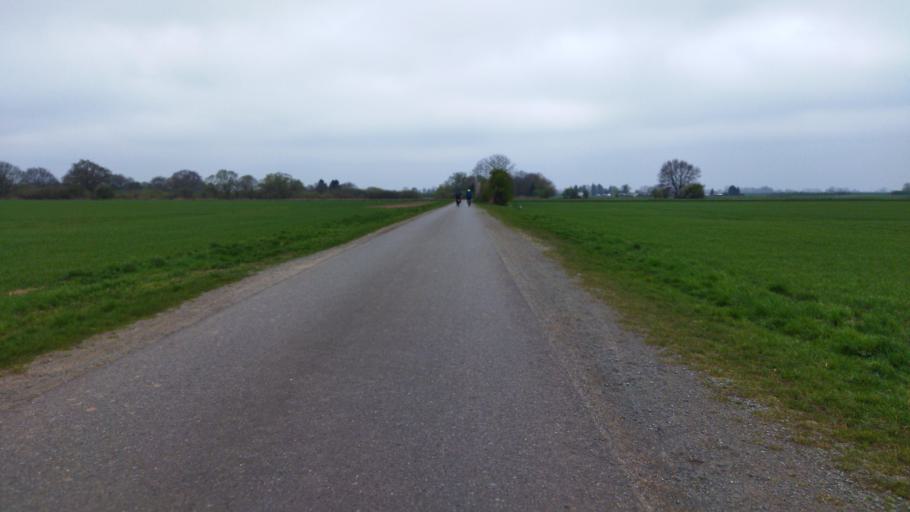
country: DE
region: Lower Saxony
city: Riede
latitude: 53.0116
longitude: 8.9649
